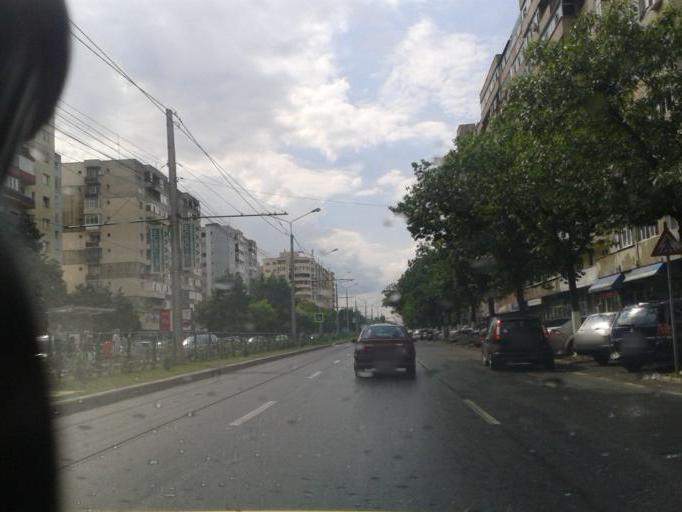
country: RO
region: Prahova
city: Ploiesti
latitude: 44.9502
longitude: 26.0037
